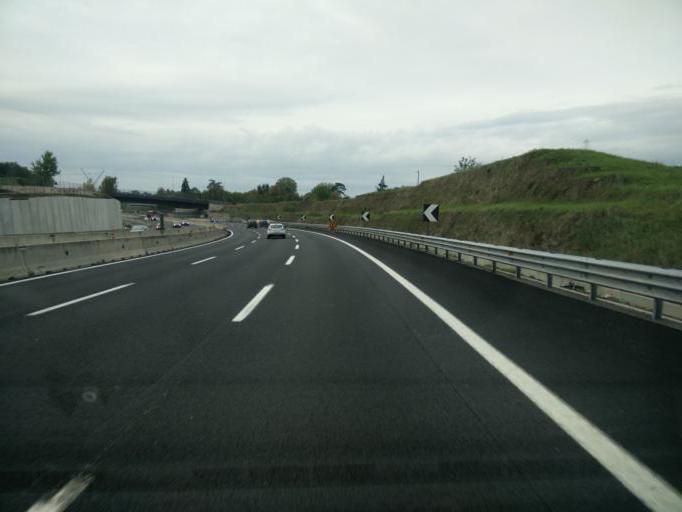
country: IT
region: Tuscany
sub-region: Province of Florence
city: Scandicci
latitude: 43.7432
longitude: 11.1804
